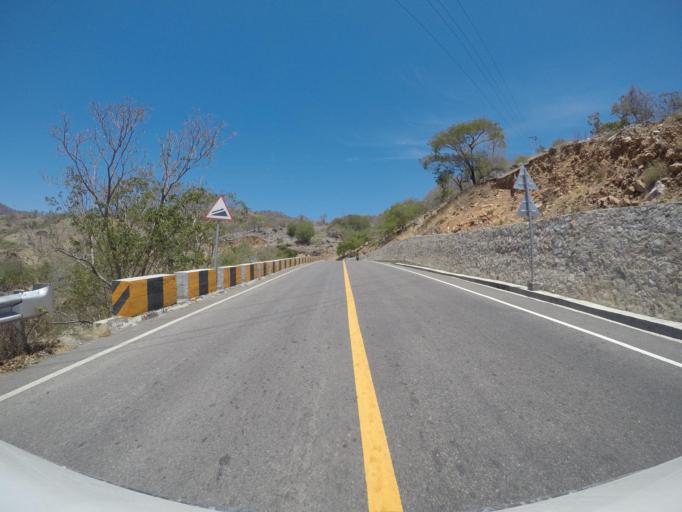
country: TL
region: Manatuto
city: Manatuto
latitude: -8.4908
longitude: 125.9650
